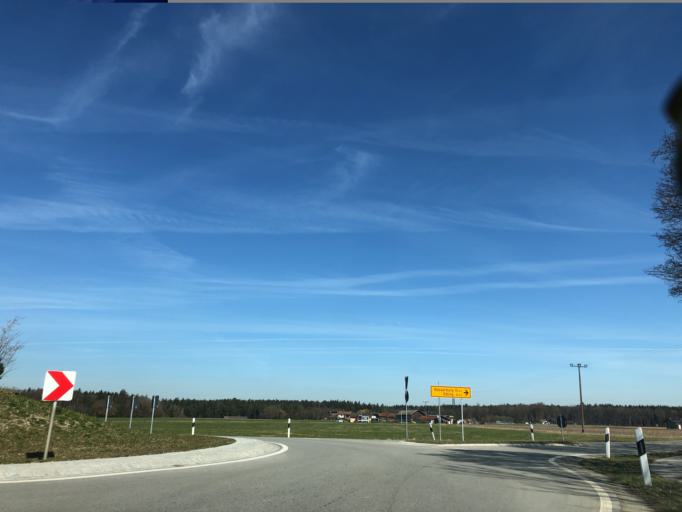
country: DE
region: Bavaria
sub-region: Upper Bavaria
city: Pfaffing
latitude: 48.0618
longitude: 12.1112
